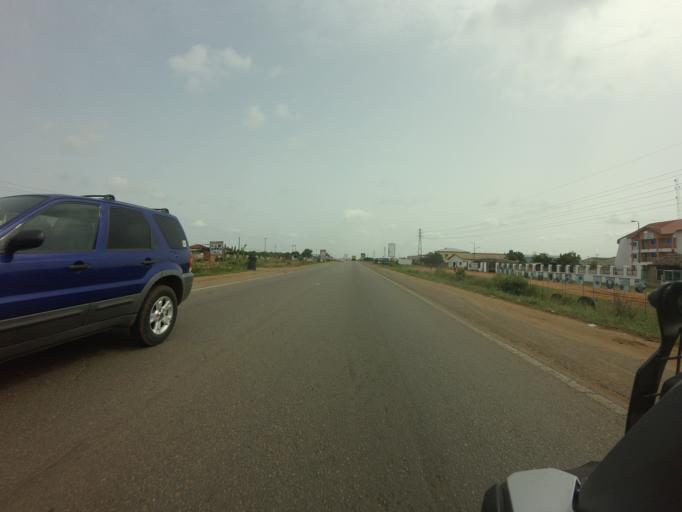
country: GH
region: Greater Accra
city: Tema
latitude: 5.7459
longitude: 0.0394
